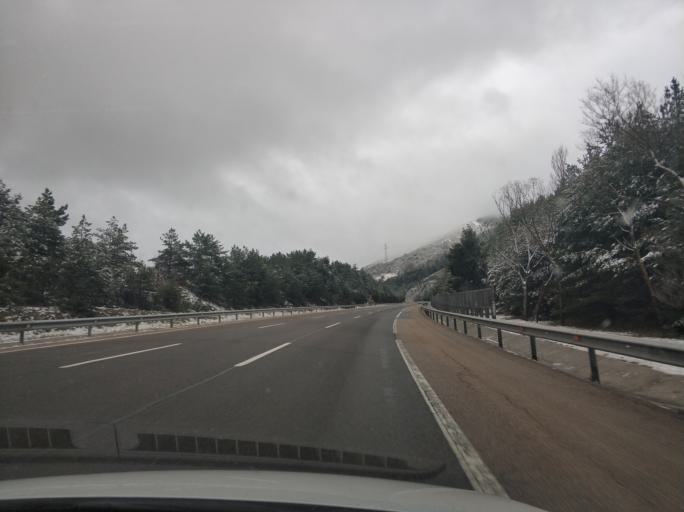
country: ES
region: Madrid
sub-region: Provincia de Madrid
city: Somosierra
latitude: 41.1675
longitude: -3.5828
